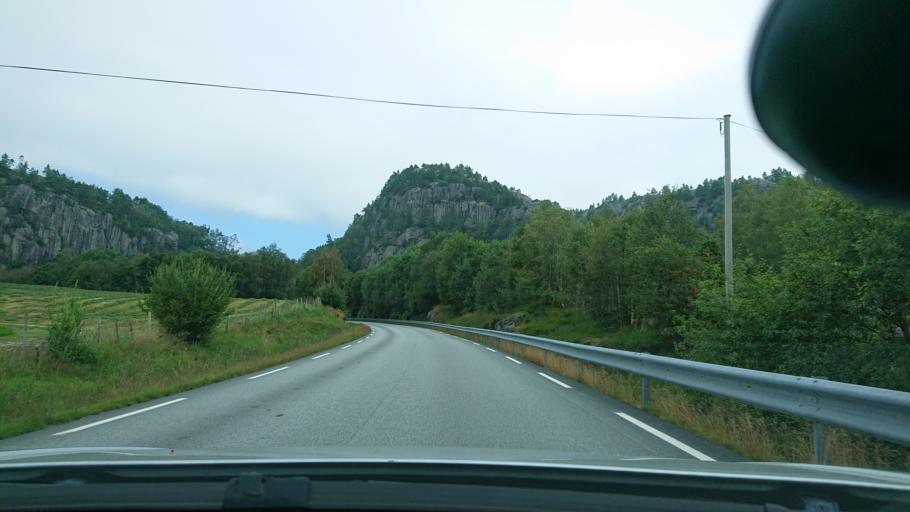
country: NO
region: Rogaland
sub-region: Hjelmeland
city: Hjelmelandsvagen
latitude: 59.2193
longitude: 6.2291
